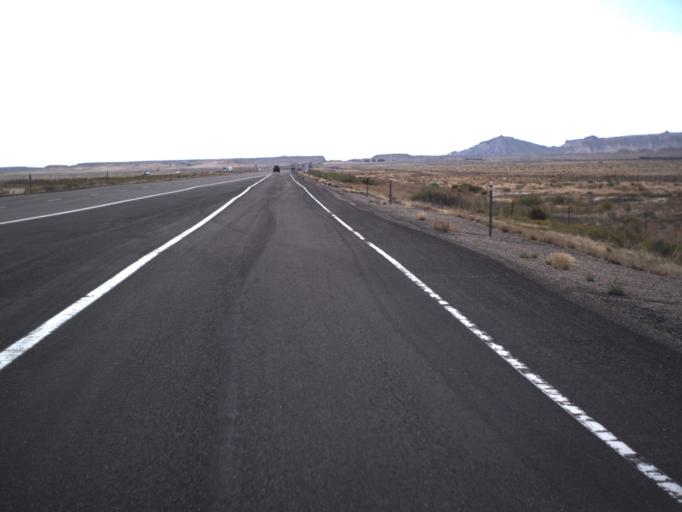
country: US
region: Utah
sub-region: Grand County
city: Moab
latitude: 38.9546
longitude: -109.7582
